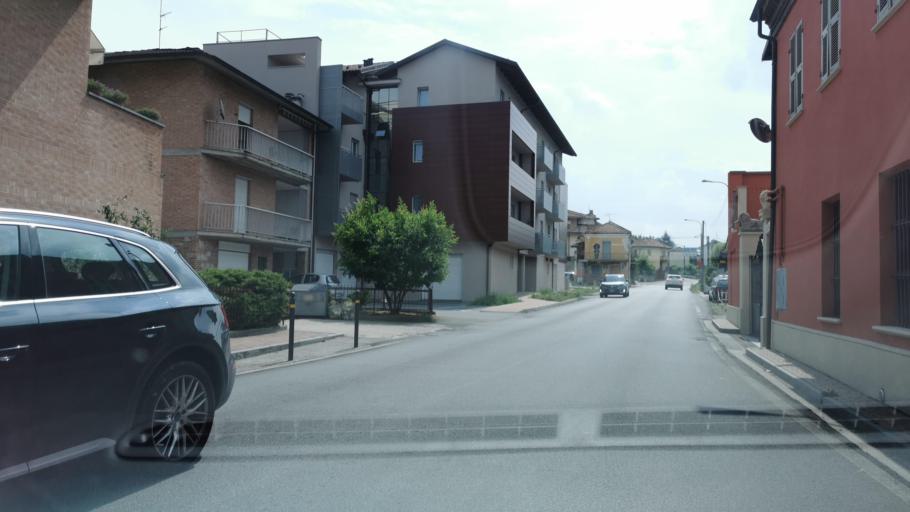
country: IT
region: Piedmont
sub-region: Provincia di Cuneo
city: Grinzane Cavour
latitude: 44.6553
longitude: 7.9803
